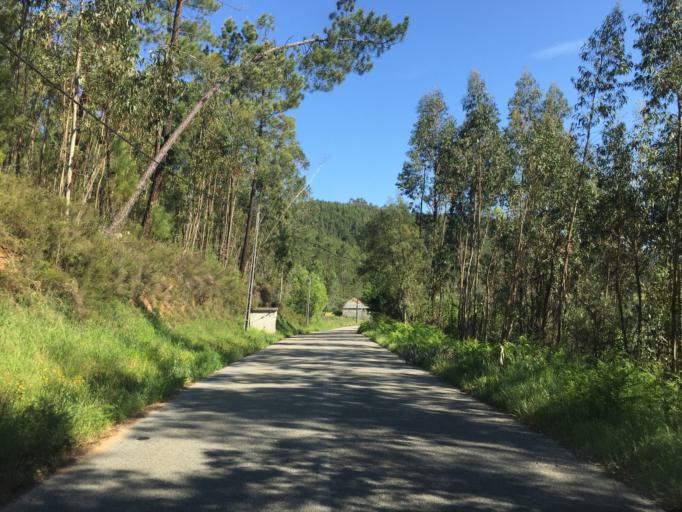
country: PT
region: Coimbra
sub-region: Pampilhosa da Serra
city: Pampilhosa da Serra
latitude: 40.0486
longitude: -7.8113
